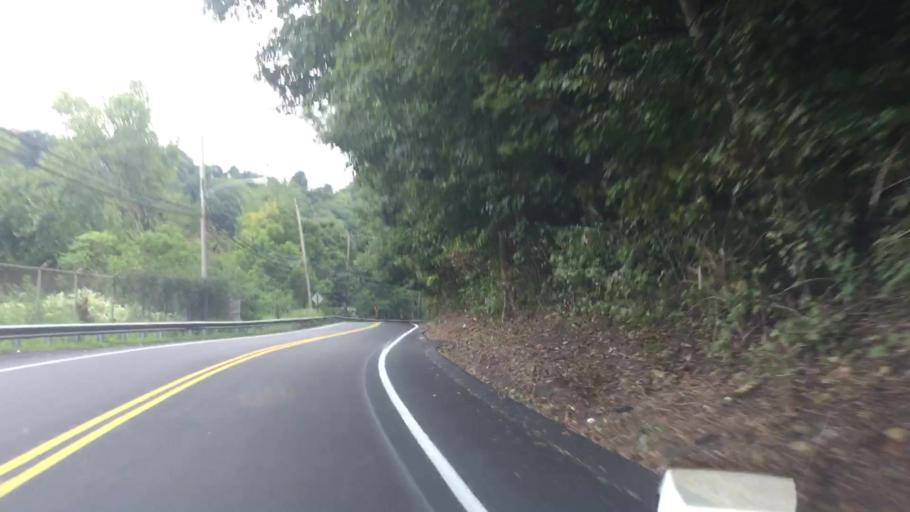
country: US
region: Pennsylvania
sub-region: Allegheny County
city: Carnegie
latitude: 40.4137
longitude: -80.0960
